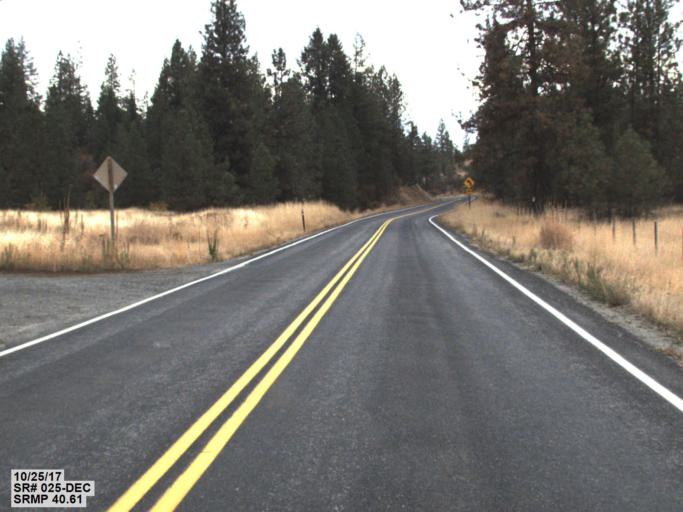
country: US
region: Washington
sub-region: Lincoln County
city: Davenport
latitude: 48.1052
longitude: -118.2041
